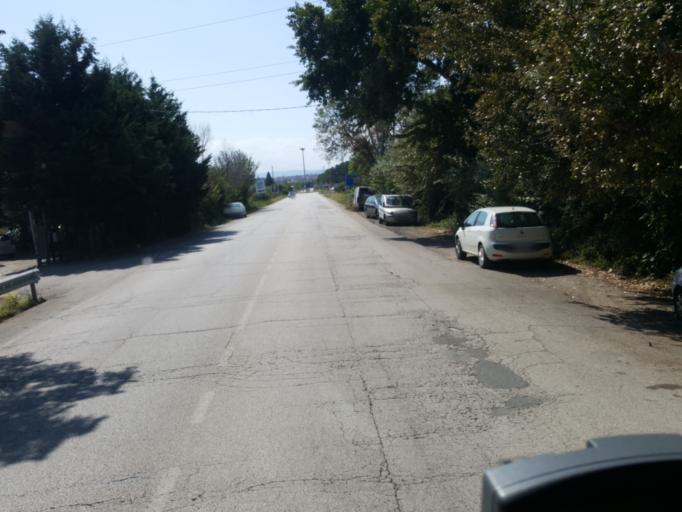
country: IT
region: Abruzzo
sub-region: Provincia di Chieti
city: Salvo Marina
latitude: 42.0584
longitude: 14.7601
